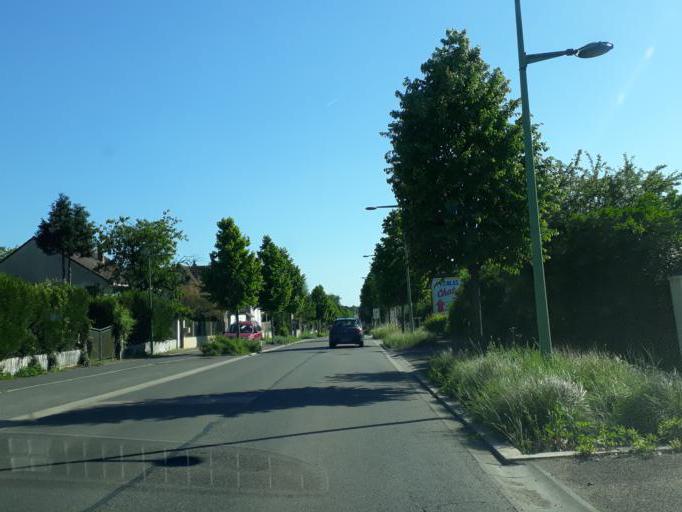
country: FR
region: Bourgogne
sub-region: Departement de la Nievre
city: Cosne-Cours-sur-Loire
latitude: 47.4210
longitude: 2.9301
